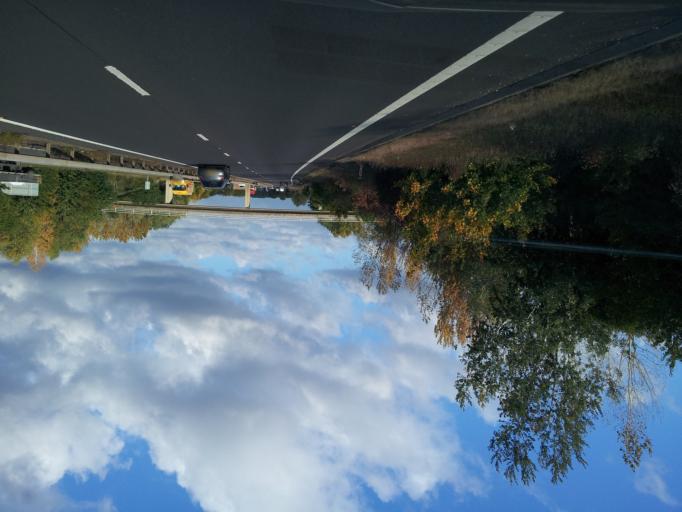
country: GB
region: England
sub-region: Bedford
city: Cardington
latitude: 52.1296
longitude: -0.4150
